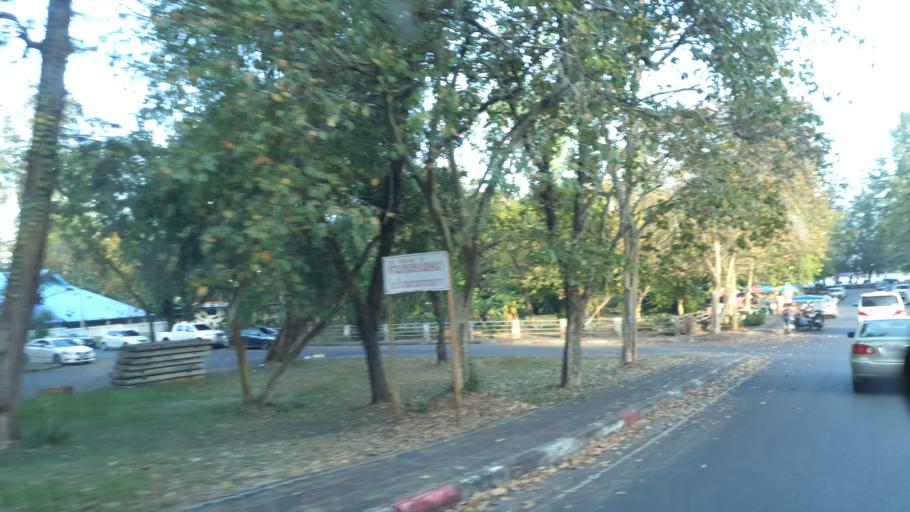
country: TH
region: Krabi
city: Krabi
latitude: 8.0534
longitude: 98.9183
